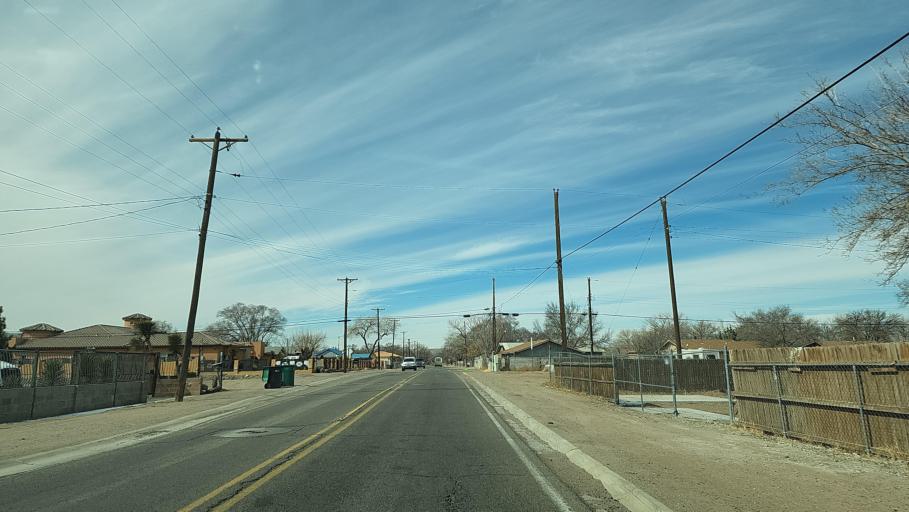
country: US
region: New Mexico
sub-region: Bernalillo County
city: South Valley
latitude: 35.0365
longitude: -106.6852
